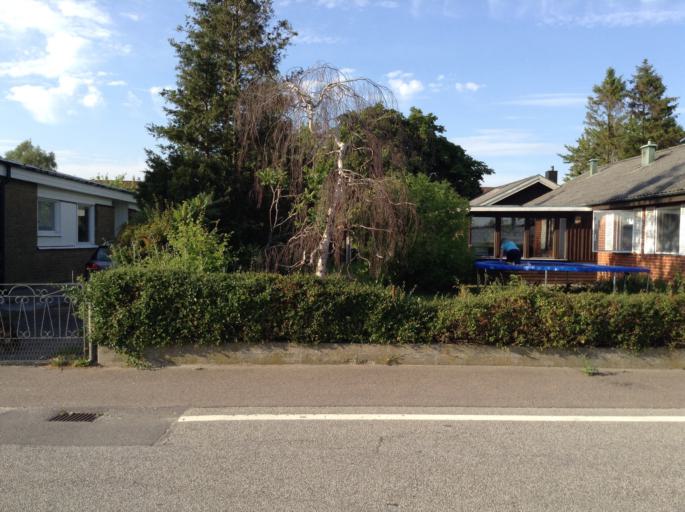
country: SE
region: Skane
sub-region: Staffanstorps Kommun
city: Hjaerup
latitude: 55.6724
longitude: 13.1367
